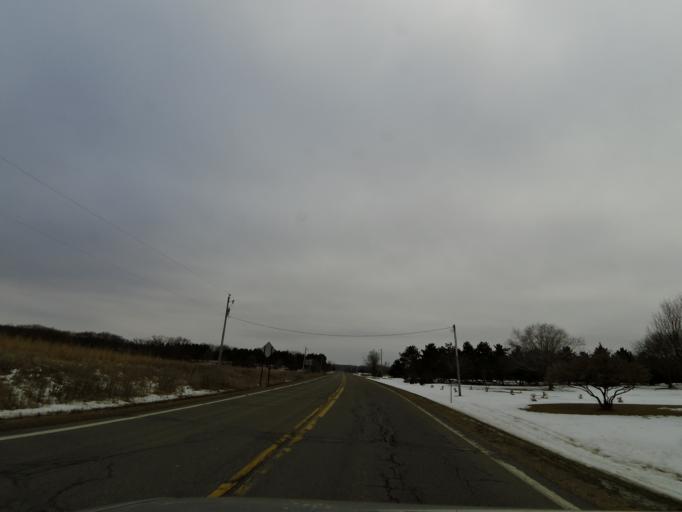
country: US
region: Minnesota
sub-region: Washington County
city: Afton
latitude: 44.8465
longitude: -92.7978
